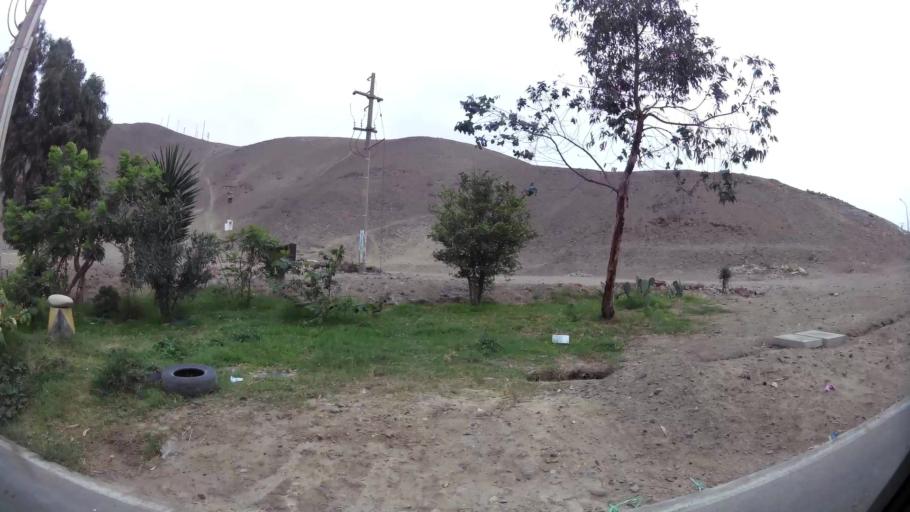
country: PE
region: Lima
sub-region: Lima
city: Santa Rosa
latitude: -11.7911
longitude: -77.1542
